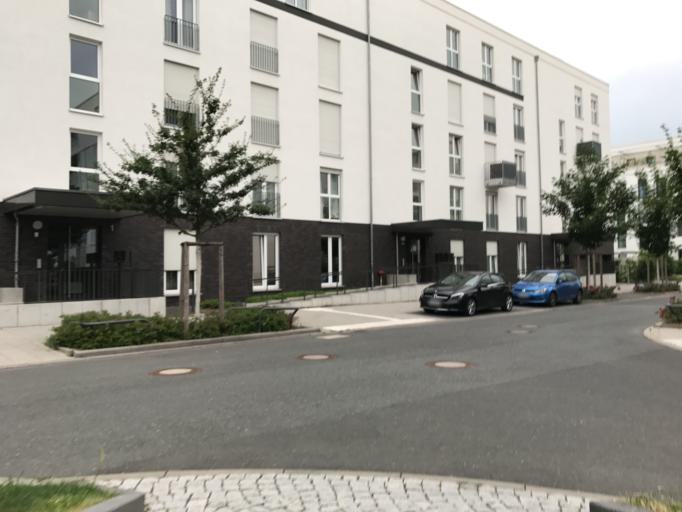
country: DE
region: Hesse
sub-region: Regierungsbezirk Darmstadt
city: Bad Homburg vor der Hoehe
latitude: 50.1776
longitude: 8.6272
